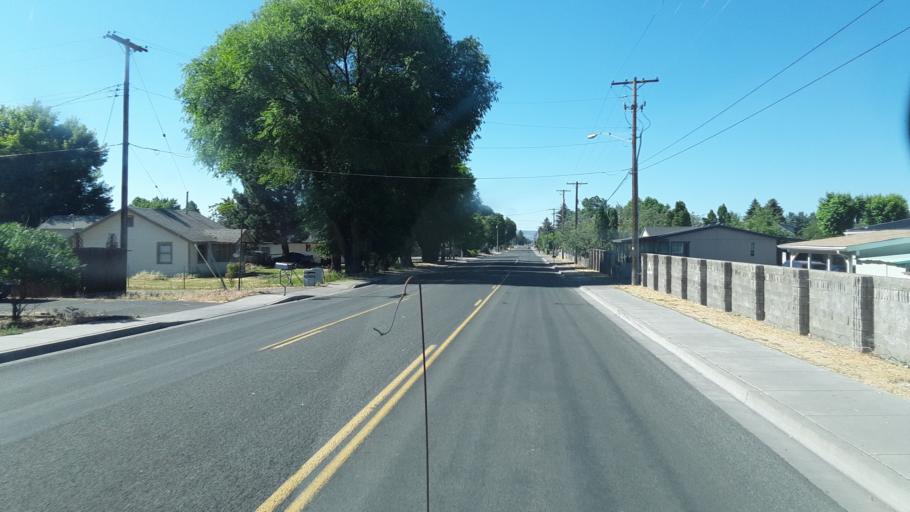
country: US
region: Oregon
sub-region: Klamath County
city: Altamont
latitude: 42.1907
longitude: -121.7228
